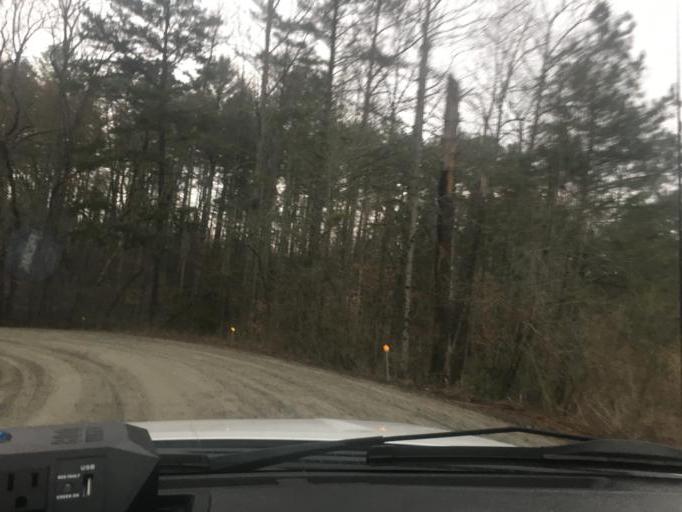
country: US
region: Georgia
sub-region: Dawson County
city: Dawsonville
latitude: 34.4415
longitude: -84.2089
